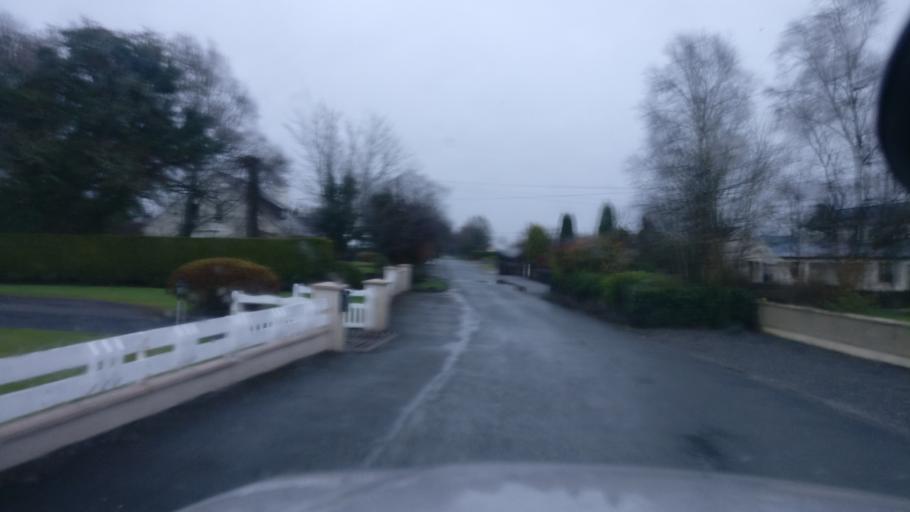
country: IE
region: Connaught
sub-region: County Galway
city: Ballinasloe
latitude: 53.3252
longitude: -8.3878
